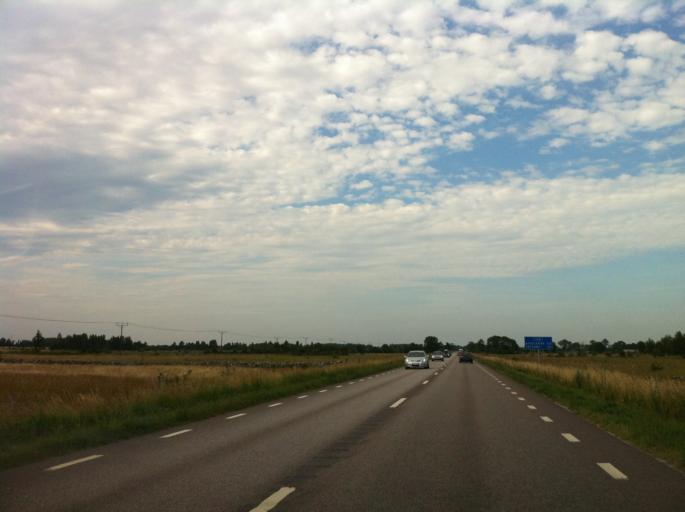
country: SE
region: Kalmar
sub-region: Borgholms Kommun
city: Borgholm
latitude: 56.9425
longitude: 16.7770
